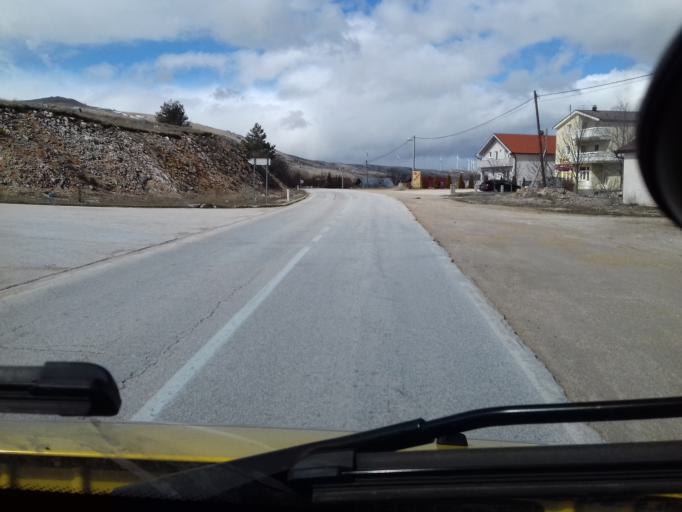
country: BA
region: Federation of Bosnia and Herzegovina
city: Dreznica
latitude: 43.5861
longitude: 17.2828
